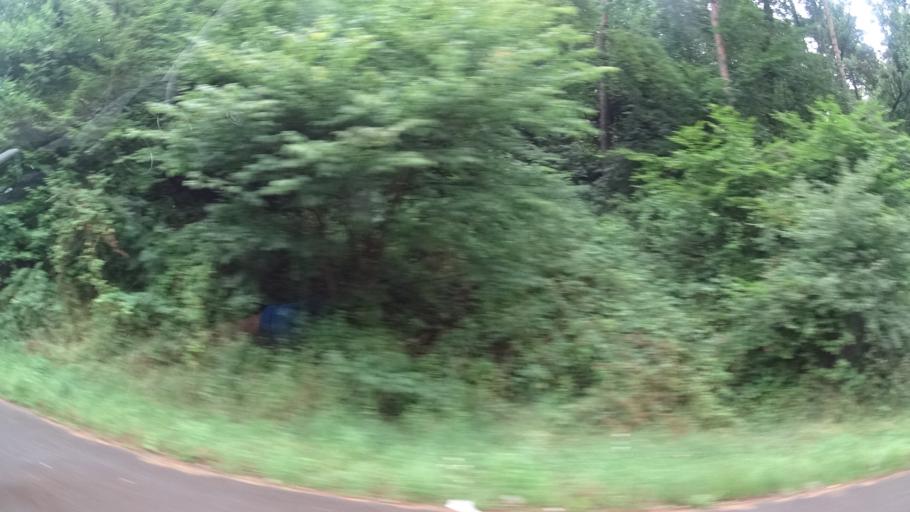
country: DE
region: Saarland
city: Dillingen
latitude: 49.3667
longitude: 6.7507
